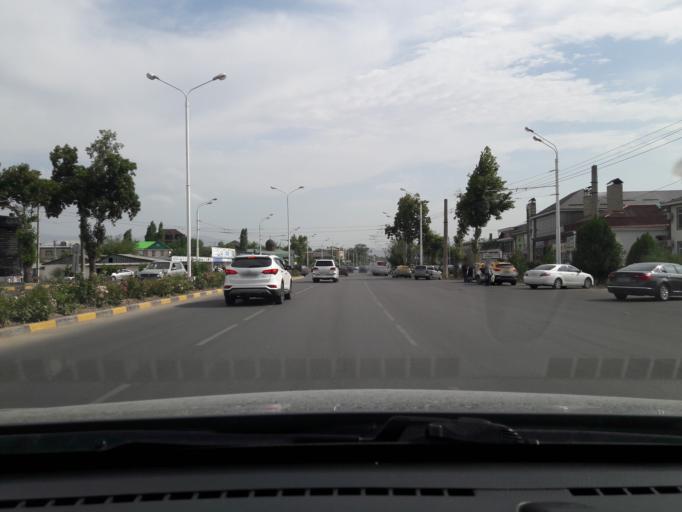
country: TJ
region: Dushanbe
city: Dushanbe
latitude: 38.5399
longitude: 68.7550
